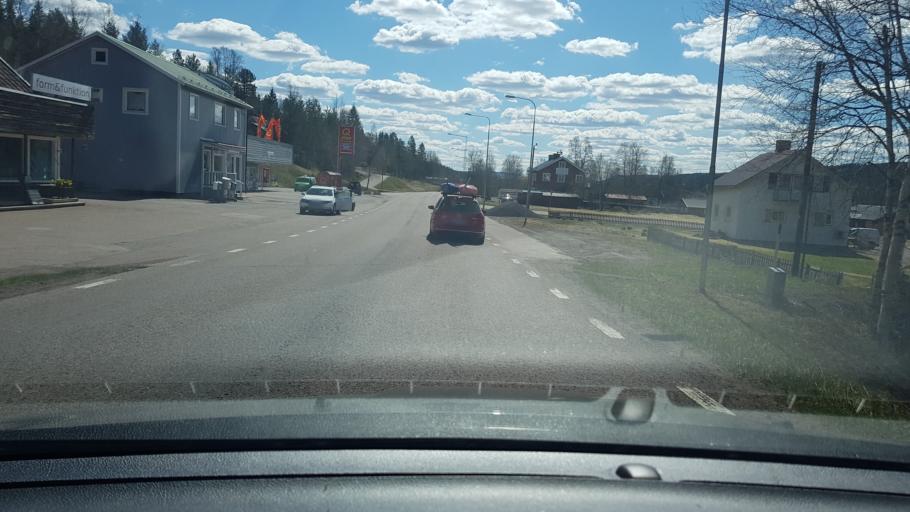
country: SE
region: Dalarna
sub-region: Malung-Saelens kommun
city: Malung
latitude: 61.1623
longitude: 13.2622
